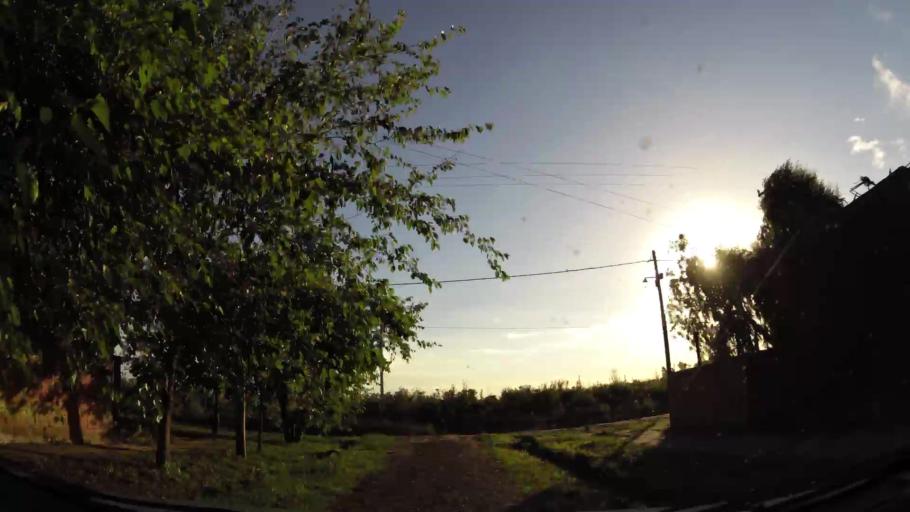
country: AR
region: Buenos Aires
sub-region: Partido de Merlo
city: Merlo
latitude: -34.6996
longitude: -58.7574
